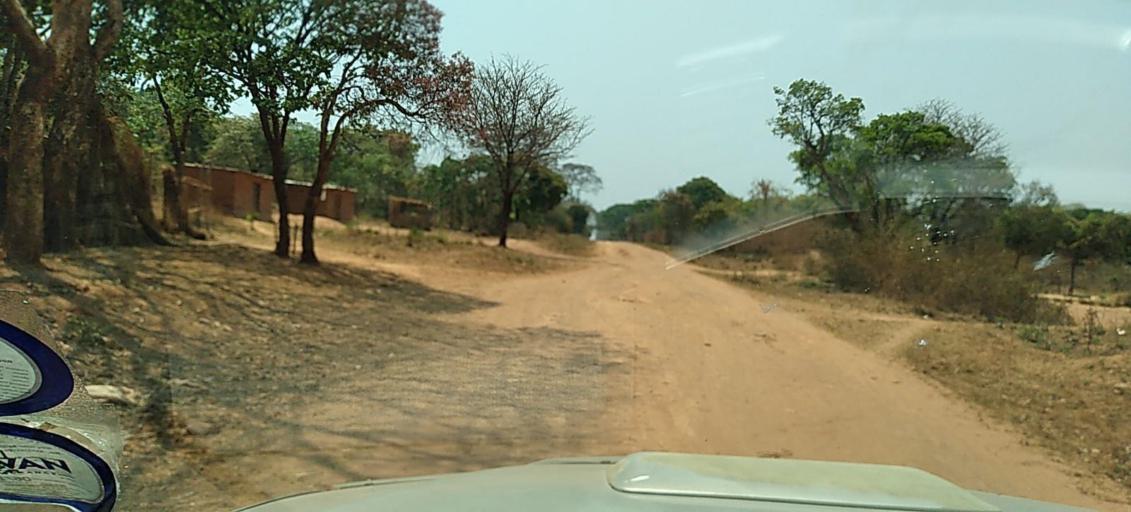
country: ZM
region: North-Western
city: Kasempa
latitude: -13.5508
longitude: 26.0268
